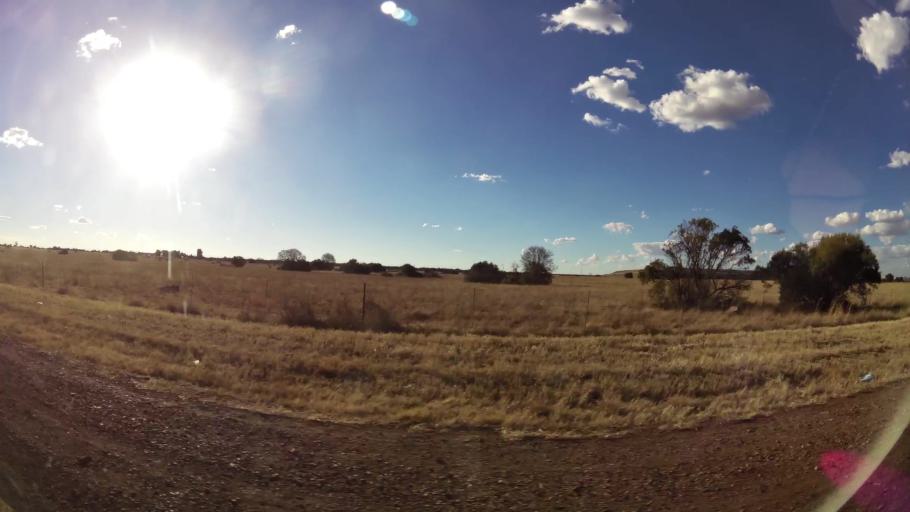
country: ZA
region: North-West
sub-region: Dr Kenneth Kaunda District Municipality
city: Stilfontein
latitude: -26.8397
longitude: 26.7634
